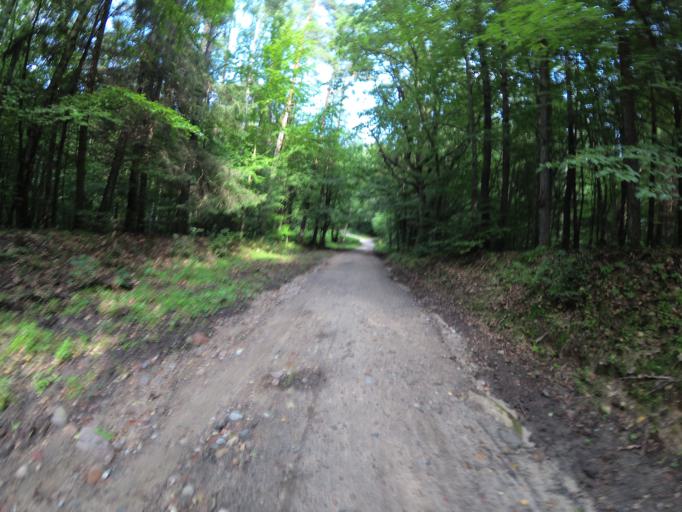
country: PL
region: Pomeranian Voivodeship
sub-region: Gdynia
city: Wielki Kack
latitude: 54.4915
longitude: 18.4730
